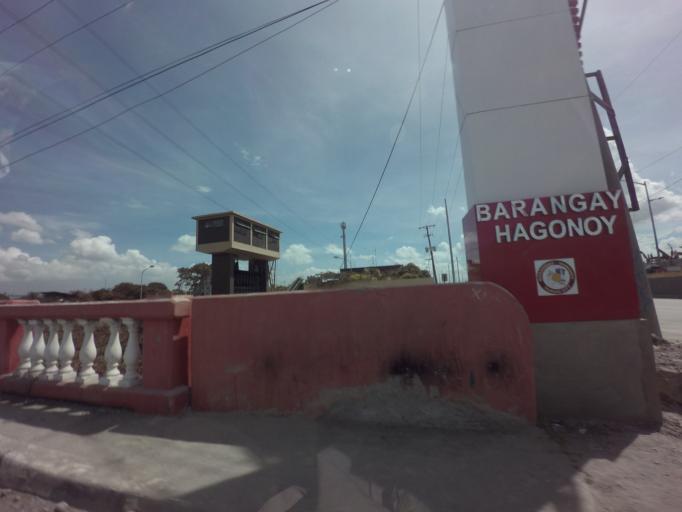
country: PH
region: Calabarzon
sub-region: Province of Rizal
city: Taguig
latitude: 14.5069
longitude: 121.0689
